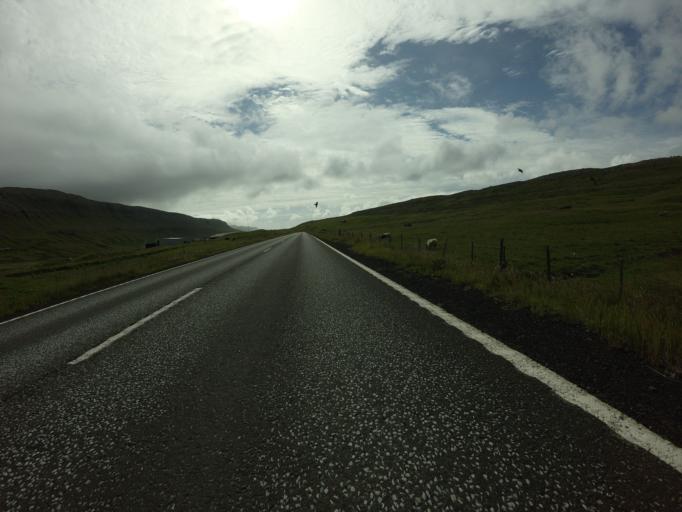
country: FO
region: Sandoy
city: Sandur
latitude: 61.8601
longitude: -6.8346
